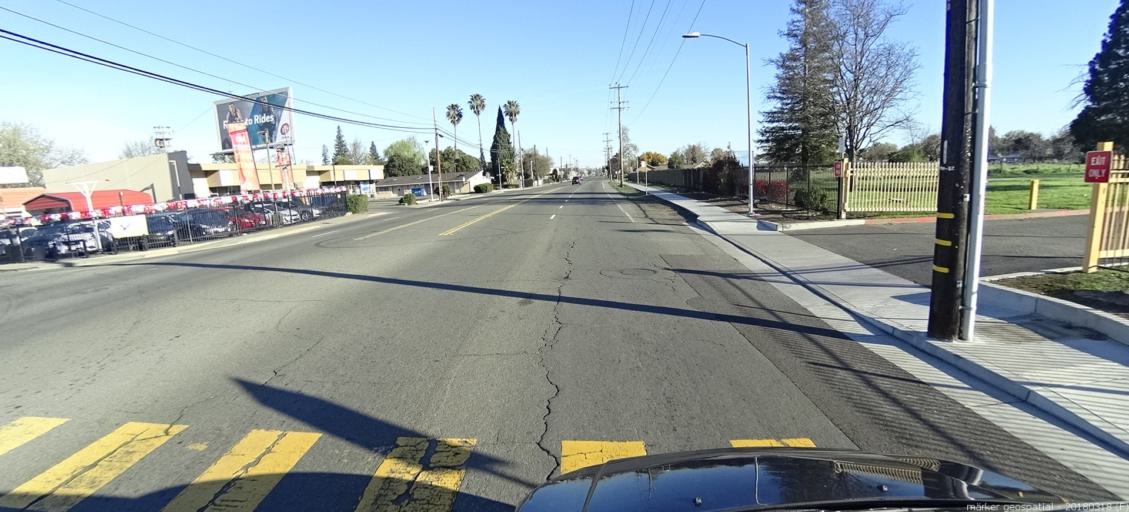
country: US
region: California
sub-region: Sacramento County
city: Parkway
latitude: 38.5200
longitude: -121.4705
